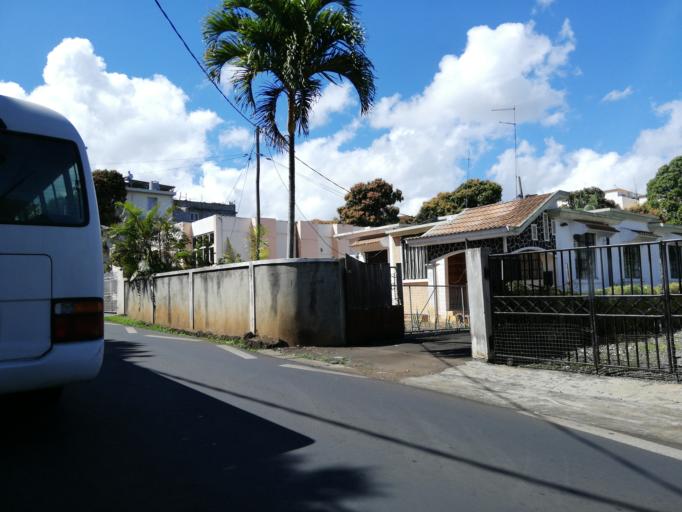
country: MU
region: Moka
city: Moka
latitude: -20.2214
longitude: 57.4656
